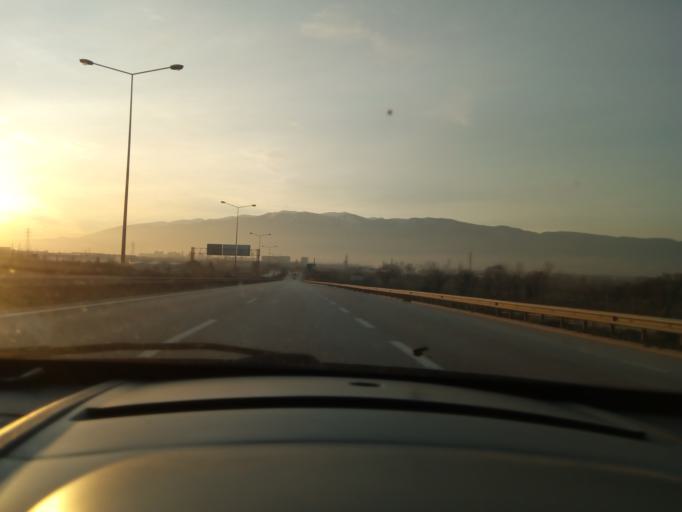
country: TR
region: Bursa
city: Demirtas
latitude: 40.2799
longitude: 29.0426
